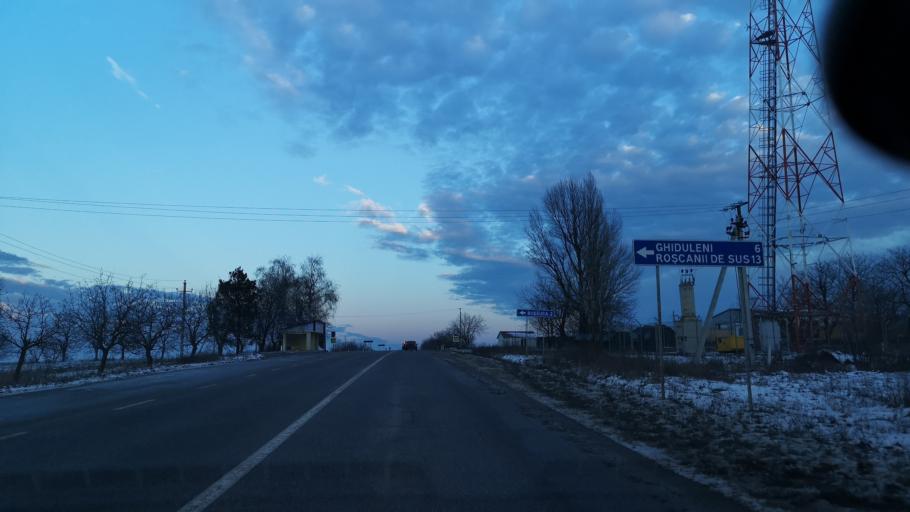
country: MD
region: Rezina
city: Saharna
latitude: 47.5822
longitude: 28.8105
